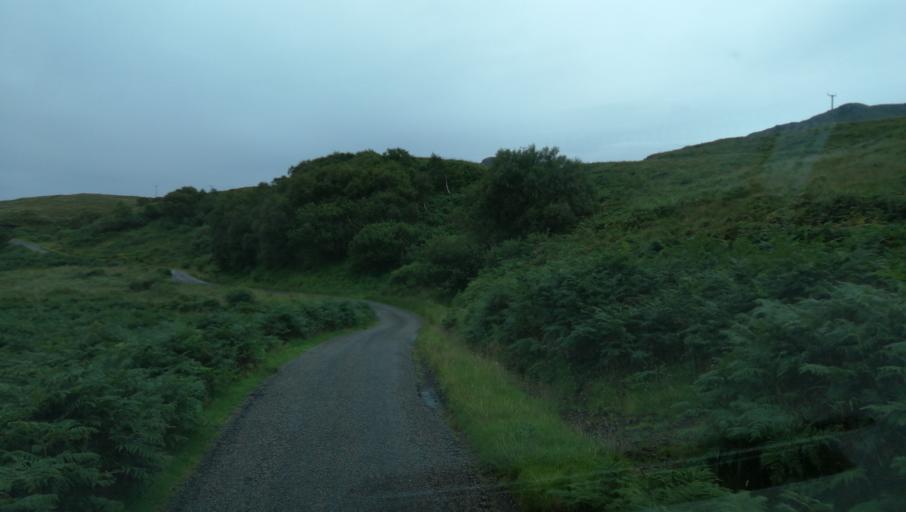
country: GB
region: Scotland
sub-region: Argyll and Bute
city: Isle Of Mull
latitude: 56.7139
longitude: -6.1474
